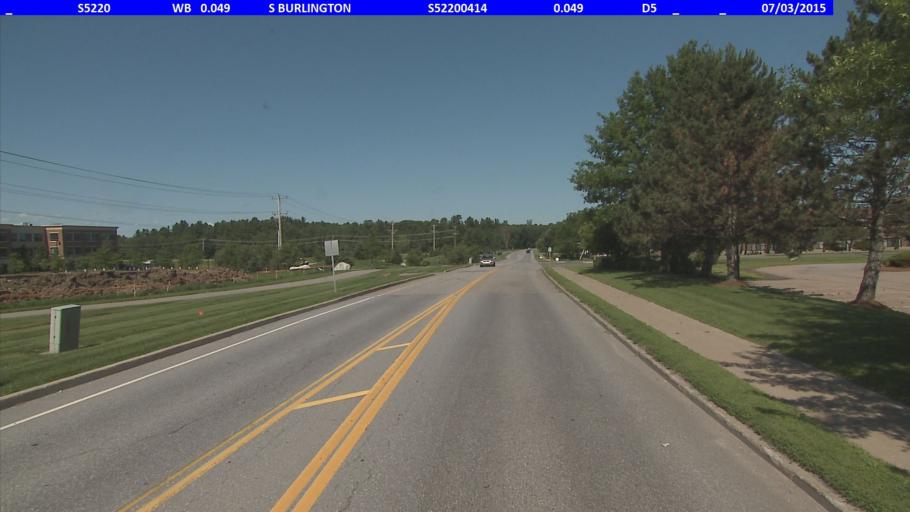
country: US
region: Vermont
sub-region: Chittenden County
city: South Burlington
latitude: 44.4537
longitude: -73.1419
